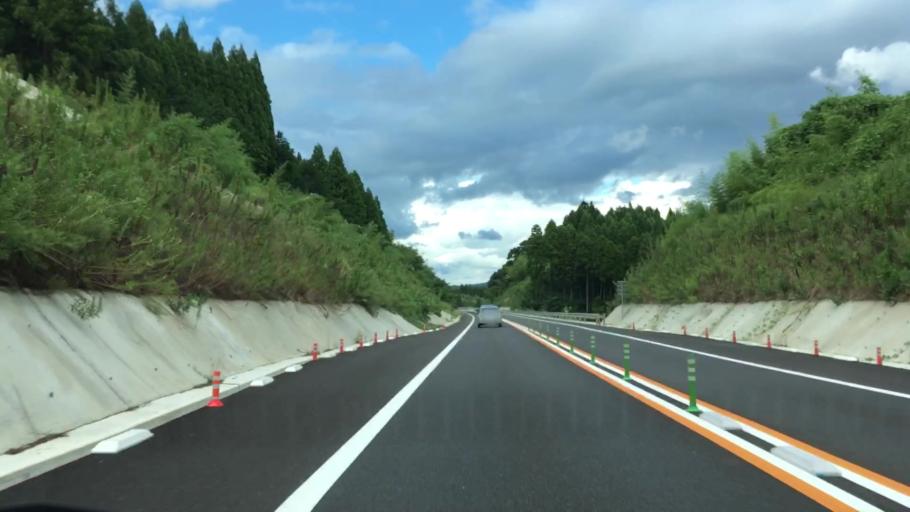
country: JP
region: Saga Prefecture
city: Imaricho-ko
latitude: 33.3159
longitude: 129.9215
